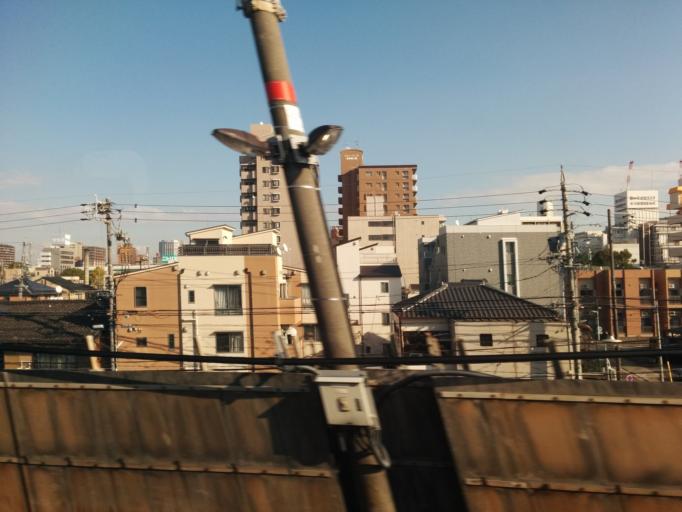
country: JP
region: Aichi
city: Nagoya-shi
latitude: 35.1459
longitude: 136.8878
